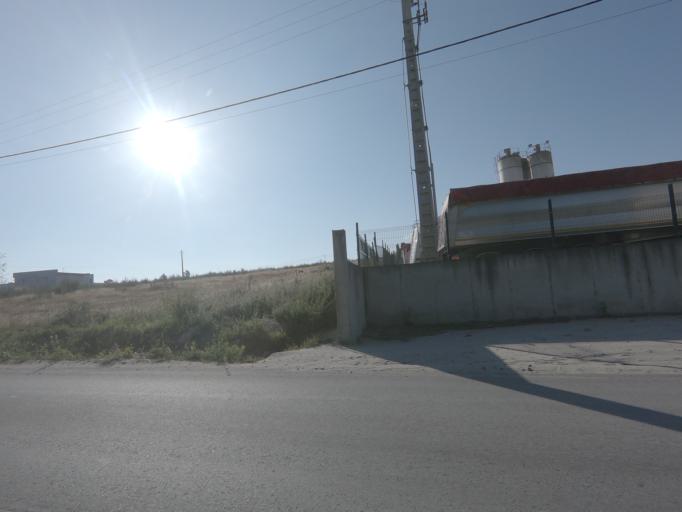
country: PT
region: Vila Real
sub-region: Chaves
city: Chaves
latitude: 41.7822
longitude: -7.4389
